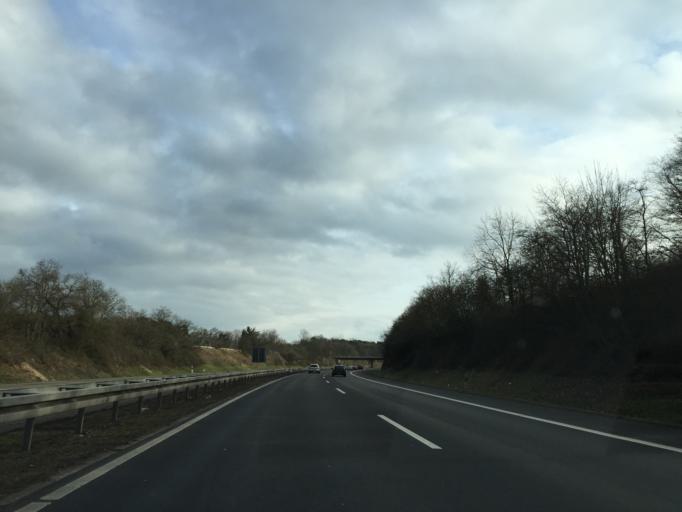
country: DE
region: Rheinland-Pfalz
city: Altrip
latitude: 49.4374
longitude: 8.5317
